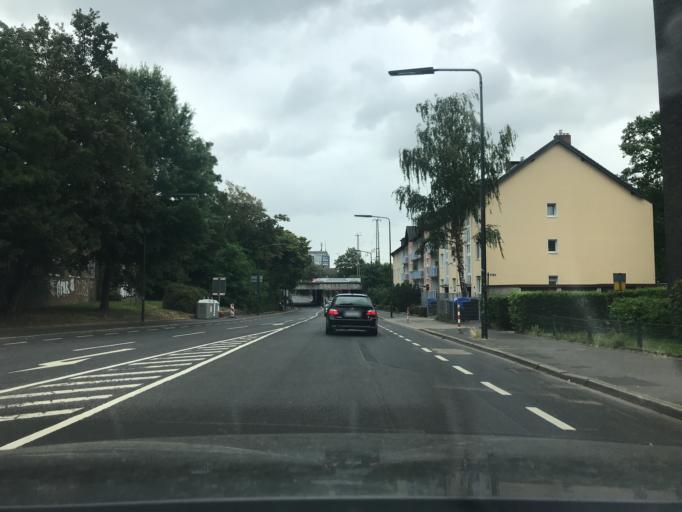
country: DE
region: North Rhine-Westphalia
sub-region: Regierungsbezirk Dusseldorf
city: Erkrath
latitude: 51.1792
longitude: 6.8596
